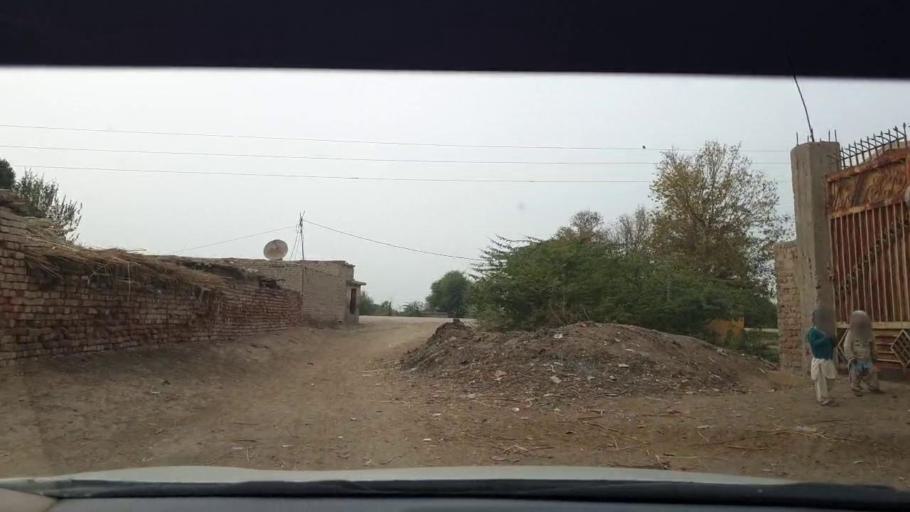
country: PK
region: Sindh
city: Berani
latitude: 25.8868
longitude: 68.8076
